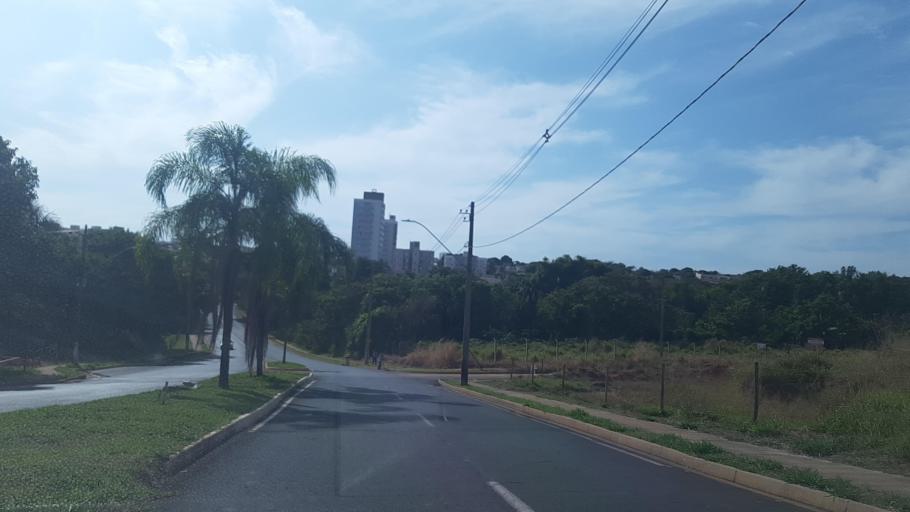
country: BR
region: Minas Gerais
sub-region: Uberlandia
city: Uberlandia
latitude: -18.8785
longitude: -48.2394
